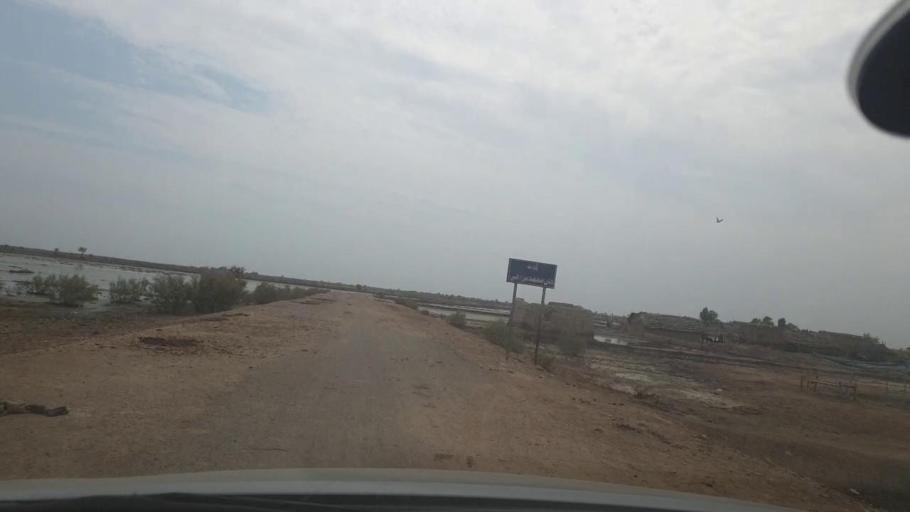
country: PK
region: Balochistan
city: Garhi Khairo
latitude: 28.0166
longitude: 68.0434
